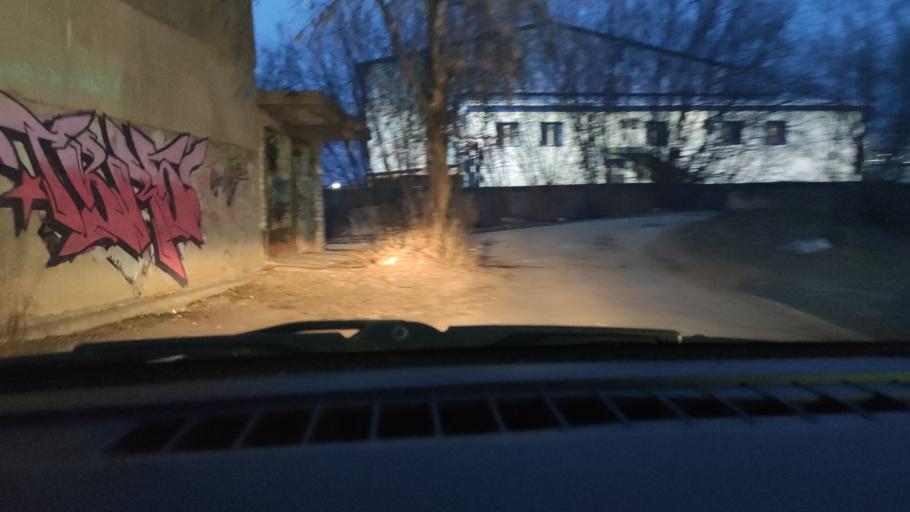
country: RU
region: Perm
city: Overyata
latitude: 58.0099
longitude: 55.9352
